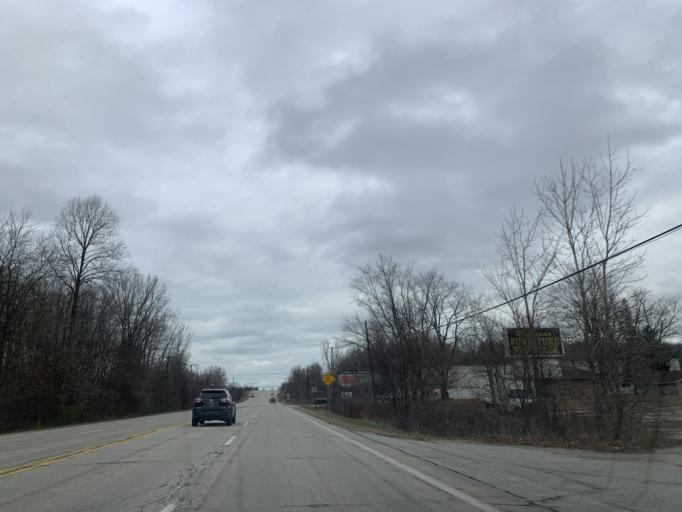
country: US
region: Indiana
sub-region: LaPorte County
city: Trail Creek
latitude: 41.7108
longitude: -86.8259
